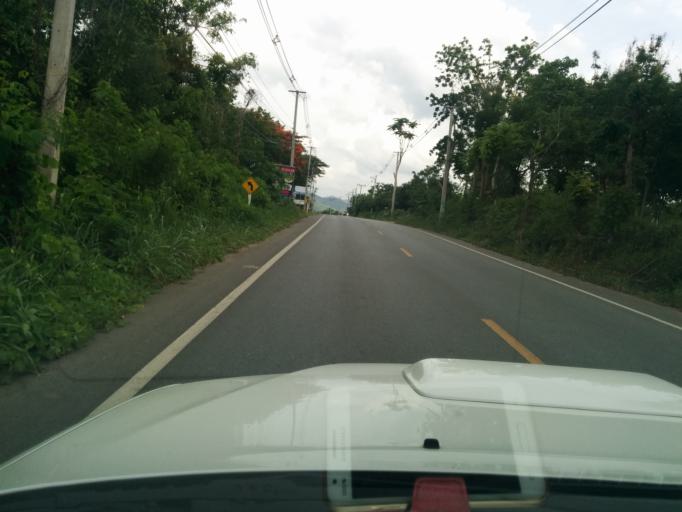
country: TH
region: Sara Buri
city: Muak Lek
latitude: 14.6117
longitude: 101.2123
